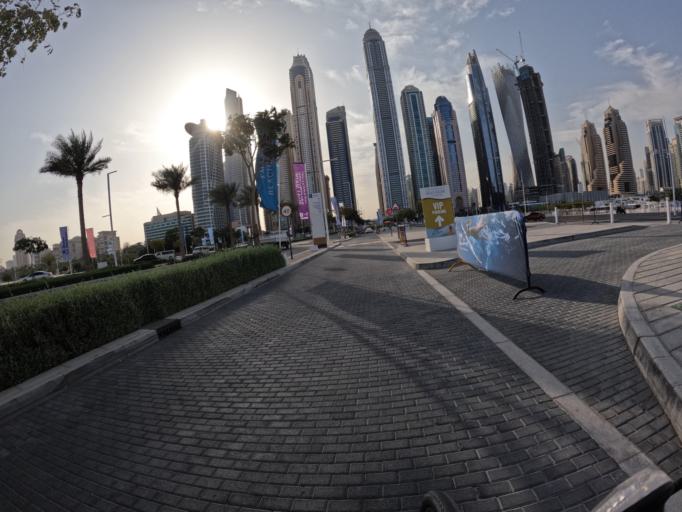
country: AE
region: Dubai
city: Dubai
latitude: 25.0925
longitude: 55.1432
